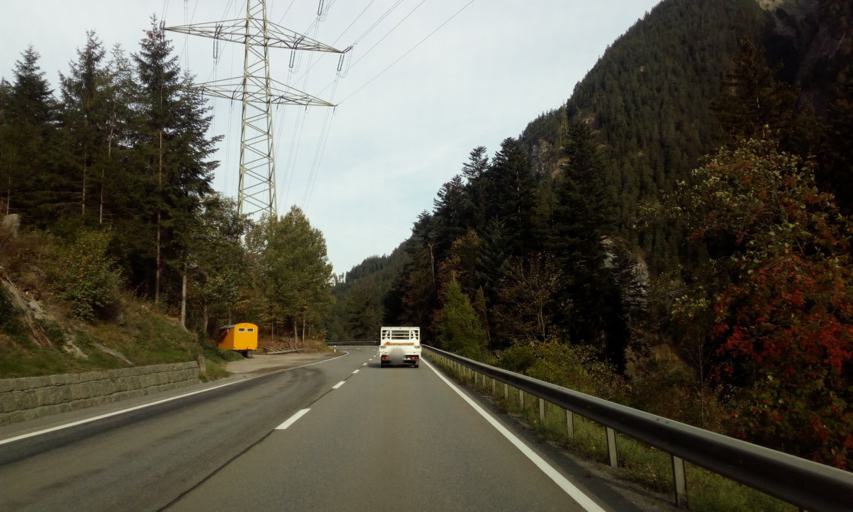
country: CH
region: Grisons
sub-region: Hinterrhein District
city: Thusis
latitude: 46.6919
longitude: 9.4939
